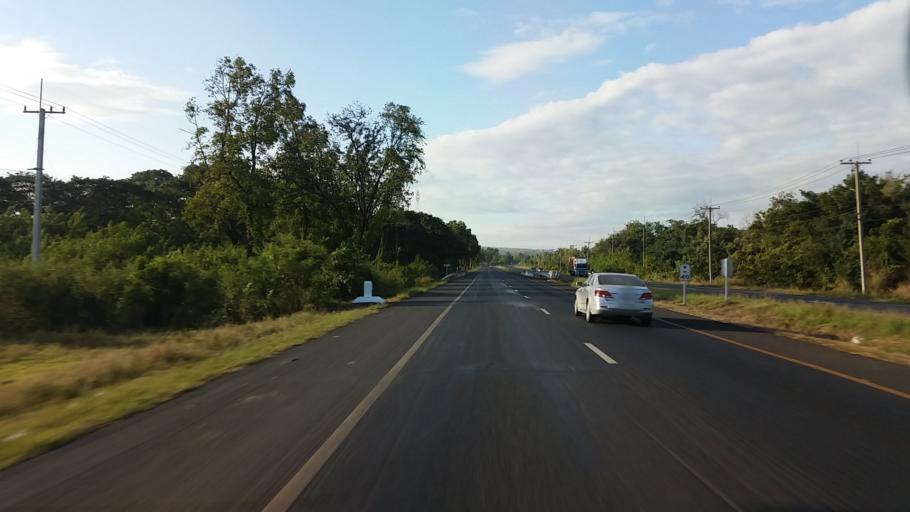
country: TH
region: Lop Buri
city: Phatthana Nikhom
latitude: 14.9970
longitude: 100.9365
